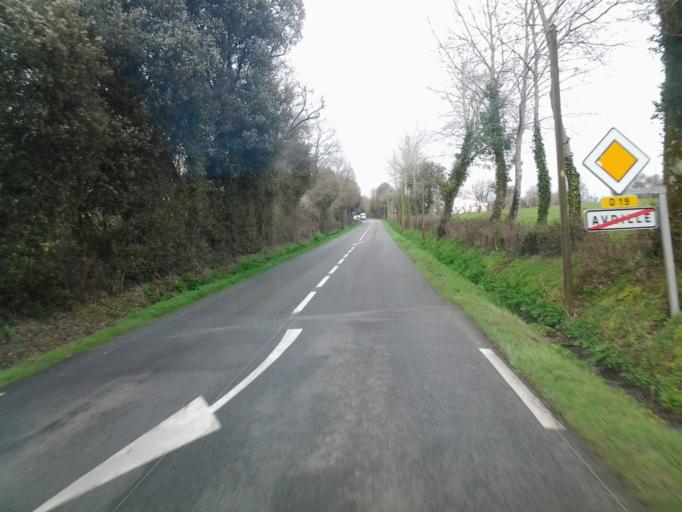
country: FR
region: Pays de la Loire
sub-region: Departement de la Vendee
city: Avrille
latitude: 46.4732
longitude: -1.4883
